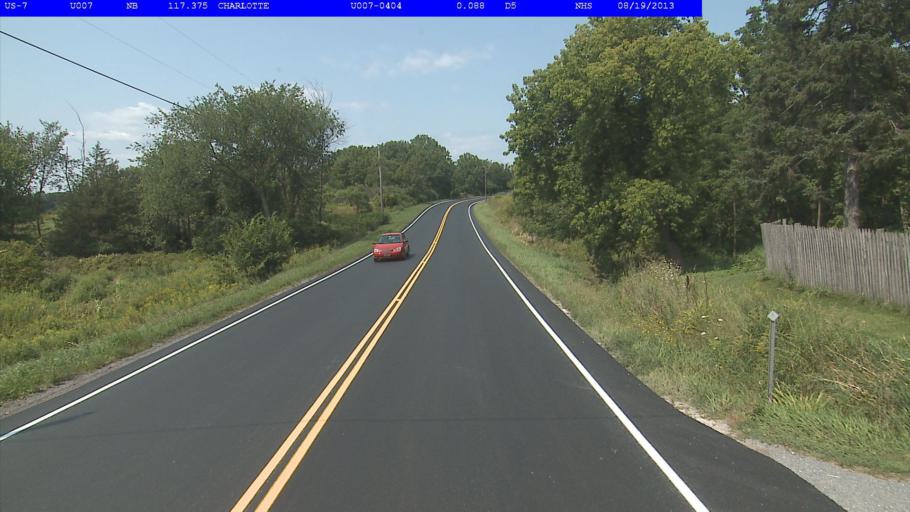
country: US
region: Vermont
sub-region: Addison County
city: Vergennes
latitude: 44.2637
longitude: -73.2311
